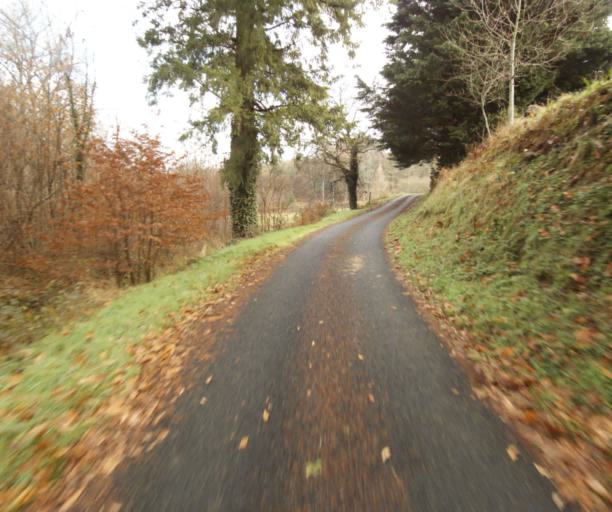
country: FR
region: Limousin
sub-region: Departement de la Correze
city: Saint-Mexant
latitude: 45.2537
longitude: 1.6414
